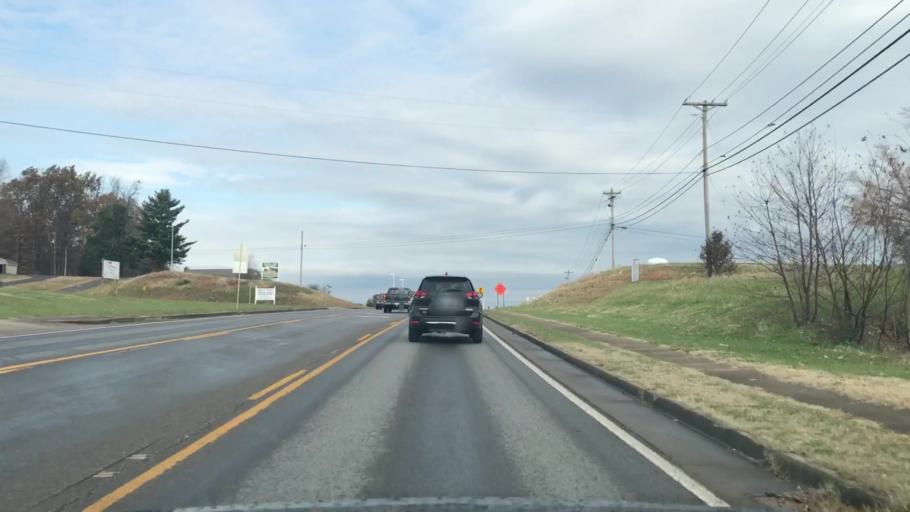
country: US
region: Kentucky
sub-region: Monroe County
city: Tompkinsville
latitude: 36.7216
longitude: -85.6873
